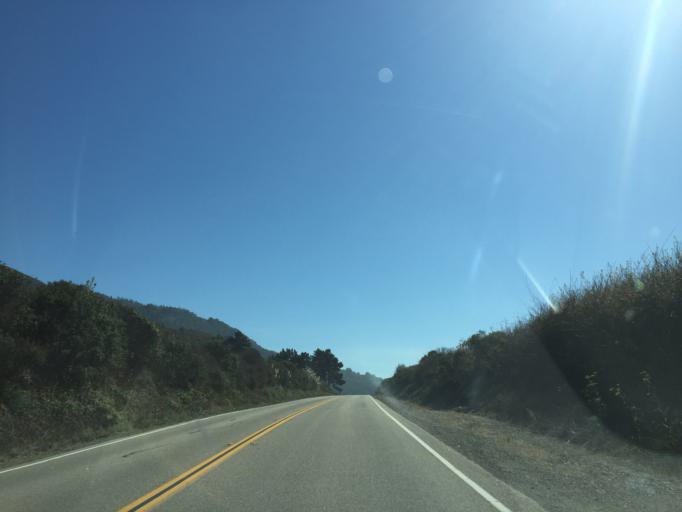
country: US
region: California
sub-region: Monterey County
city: King City
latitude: 35.9347
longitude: -121.4692
